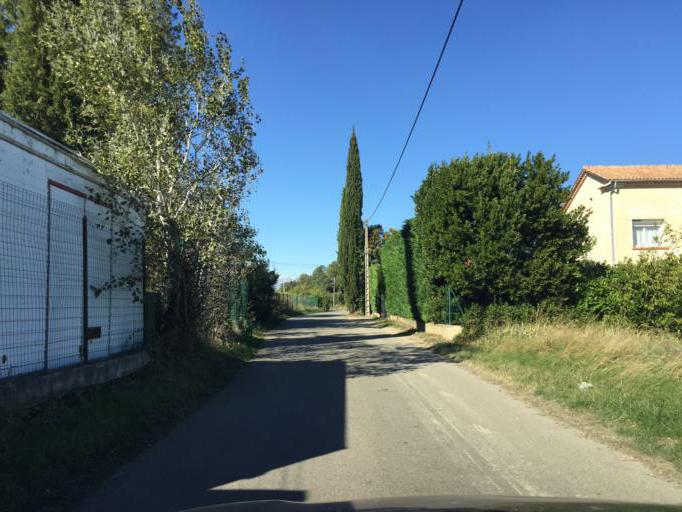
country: FR
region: Provence-Alpes-Cote d'Azur
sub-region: Departement du Vaucluse
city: Orange
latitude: 44.1615
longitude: 4.7934
